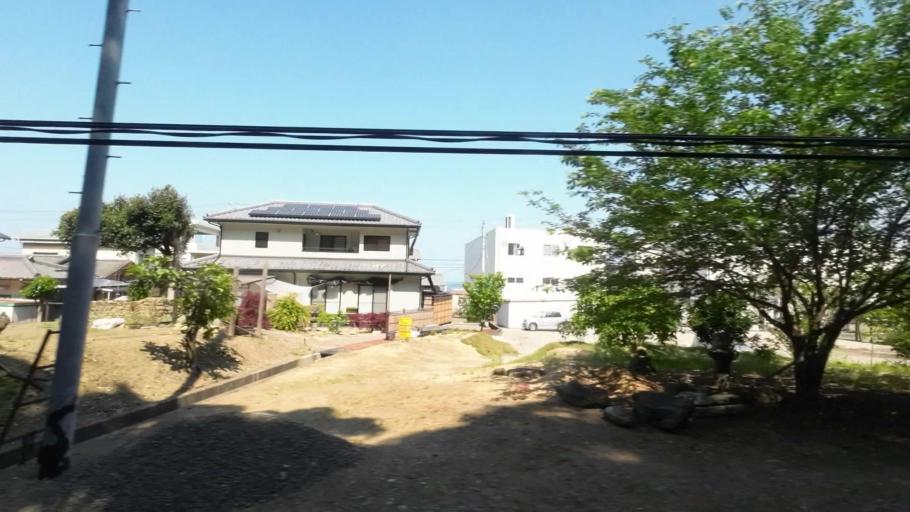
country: JP
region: Ehime
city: Kawanoecho
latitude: 34.0370
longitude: 133.5957
